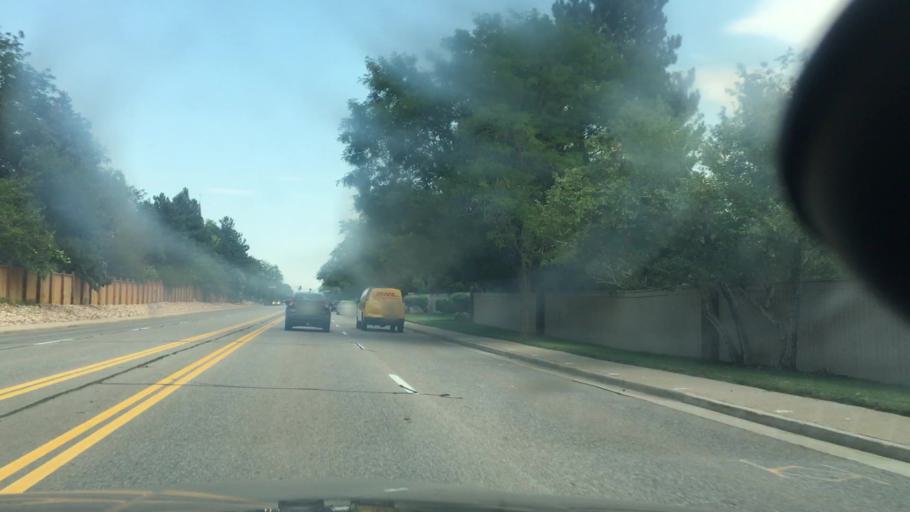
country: US
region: Colorado
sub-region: Arapahoe County
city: Castlewood
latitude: 39.5806
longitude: -104.8926
